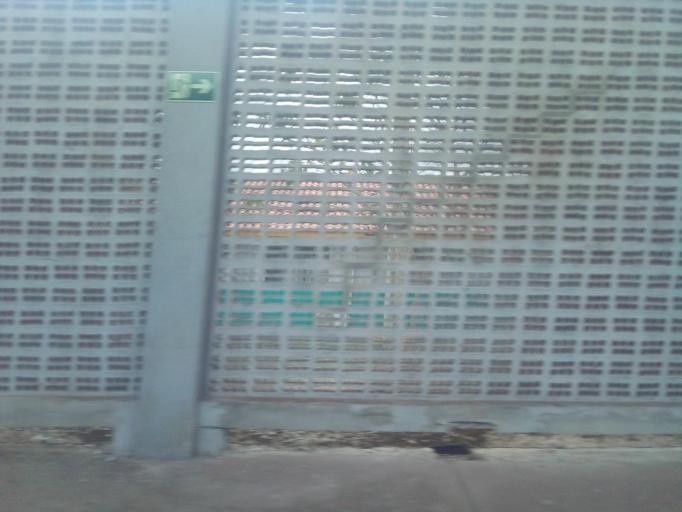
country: BR
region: Maranhao
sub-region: Santa Ines
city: Santa Ines
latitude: -3.6982
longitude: -45.4143
